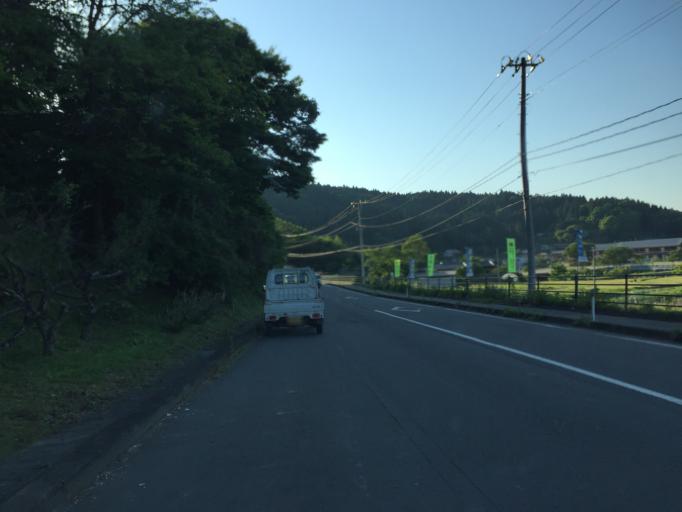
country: JP
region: Fukushima
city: Ishikawa
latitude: 36.9547
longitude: 140.4289
